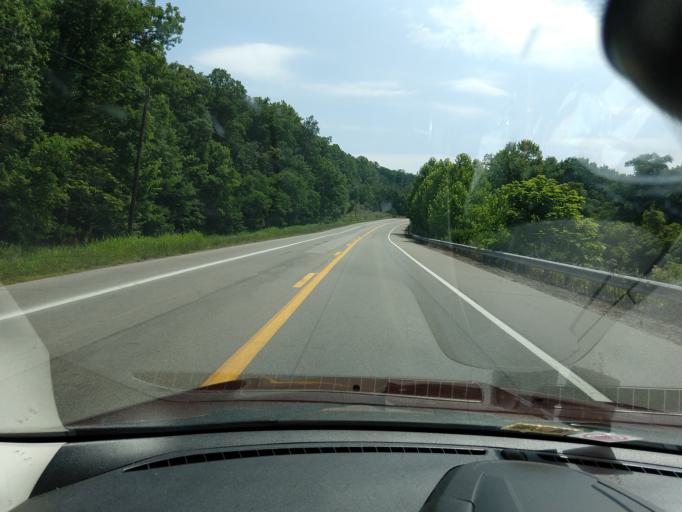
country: US
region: West Virginia
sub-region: Jackson County
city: Ravenswood
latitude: 38.8601
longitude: -81.8122
